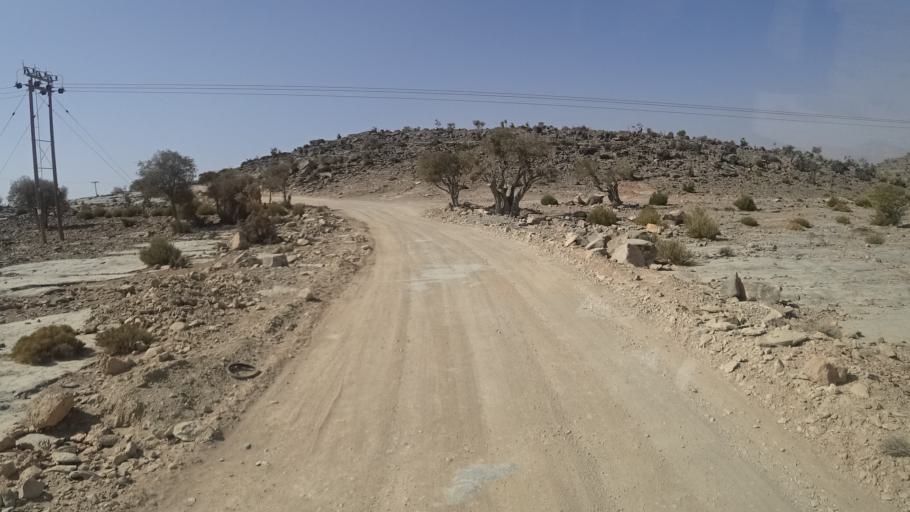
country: OM
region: Muhafazat ad Dakhiliyah
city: Bahla'
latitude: 23.2038
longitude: 57.2008
